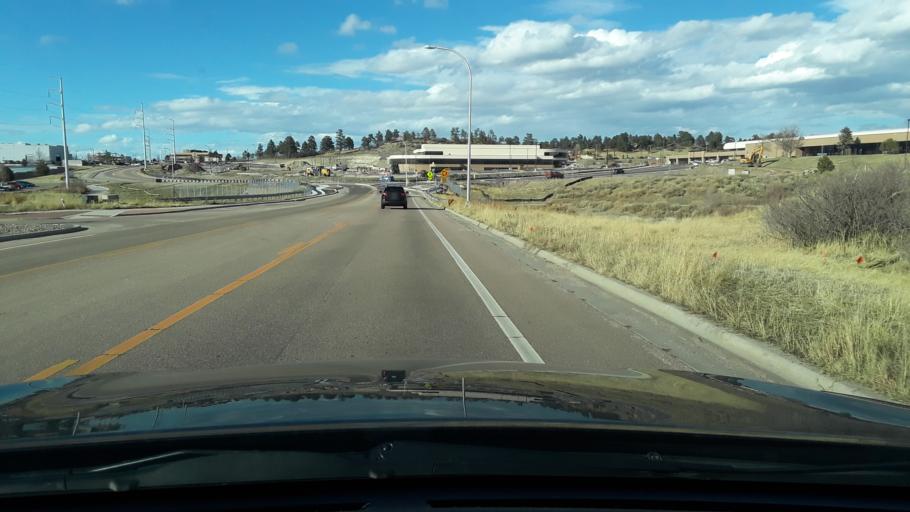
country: US
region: Colorado
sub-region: El Paso County
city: Air Force Academy
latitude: 38.9274
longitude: -104.8098
